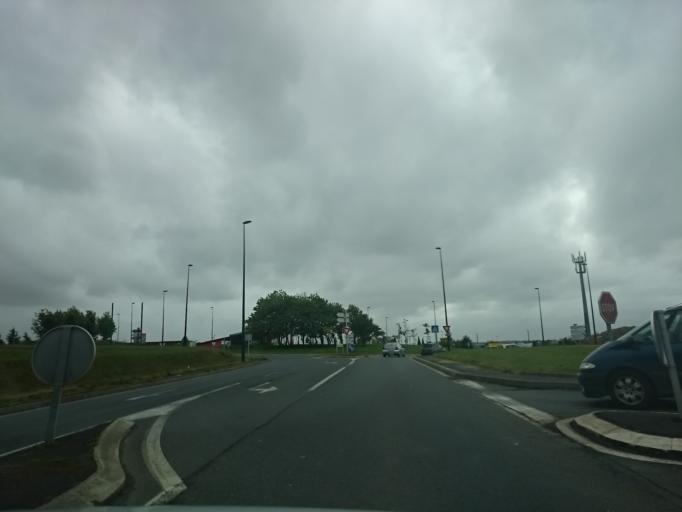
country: FR
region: Brittany
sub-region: Departement des Cotes-d'Armor
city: Lannion
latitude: 48.7359
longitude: -3.4359
